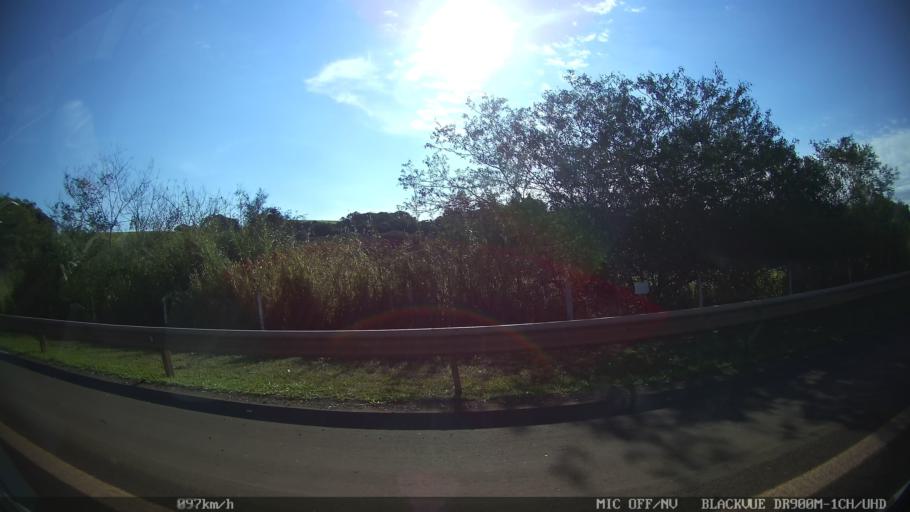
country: BR
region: Sao Paulo
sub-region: Piracicaba
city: Piracicaba
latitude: -22.6831
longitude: -47.5785
